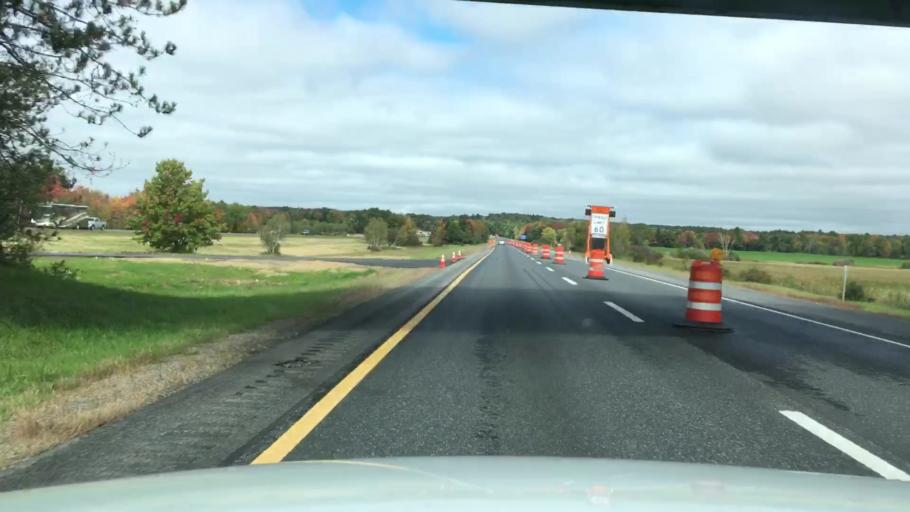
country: US
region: Maine
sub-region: Sagadahoc County
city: Richmond
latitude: 44.1503
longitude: -69.8386
